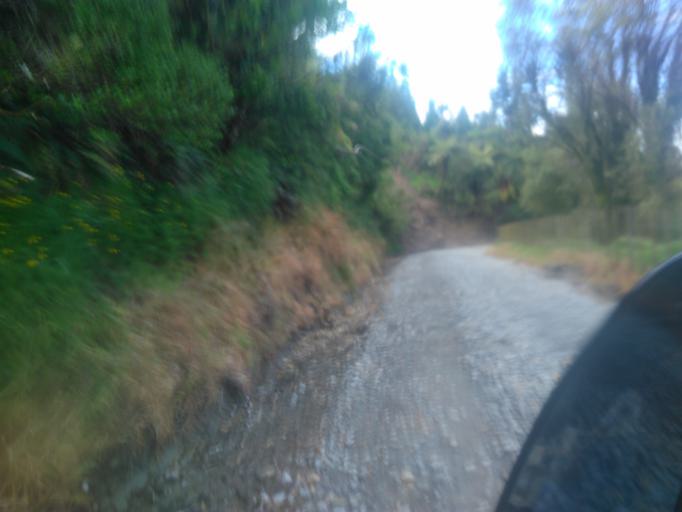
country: NZ
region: Hawke's Bay
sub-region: Wairoa District
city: Wairoa
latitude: -38.7769
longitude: 177.6299
